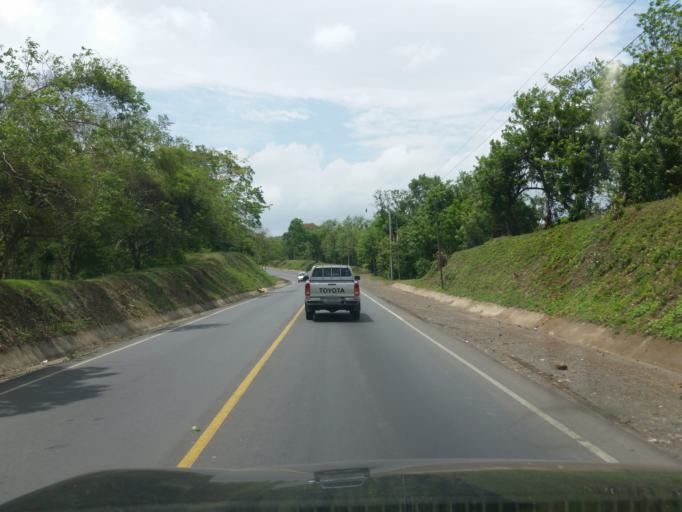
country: NI
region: Masaya
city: Catarina
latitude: 11.9240
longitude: -86.0858
